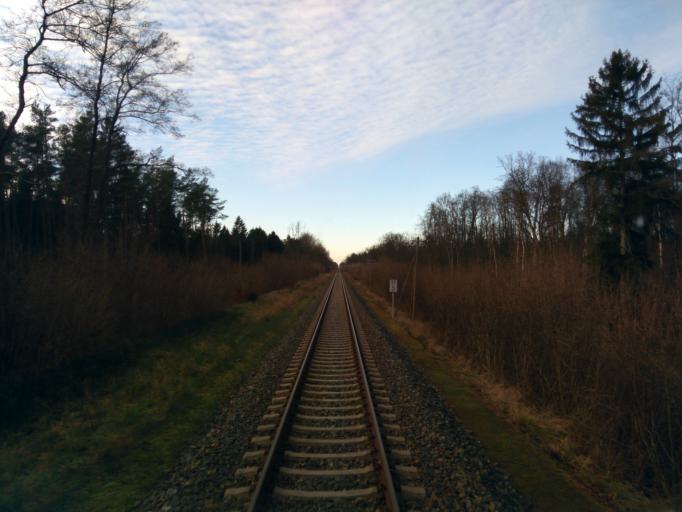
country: DE
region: Lower Saxony
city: Wriedel
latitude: 53.0090
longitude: 10.3325
